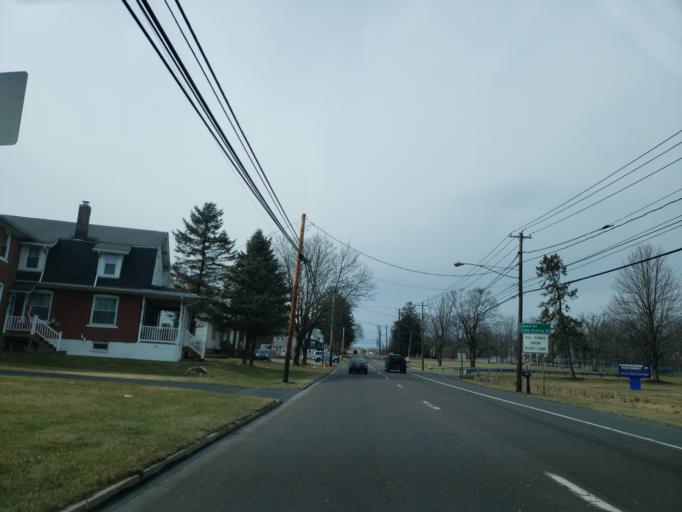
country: US
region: Pennsylvania
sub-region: Lehigh County
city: Coopersburg
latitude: 40.5313
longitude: -75.3998
